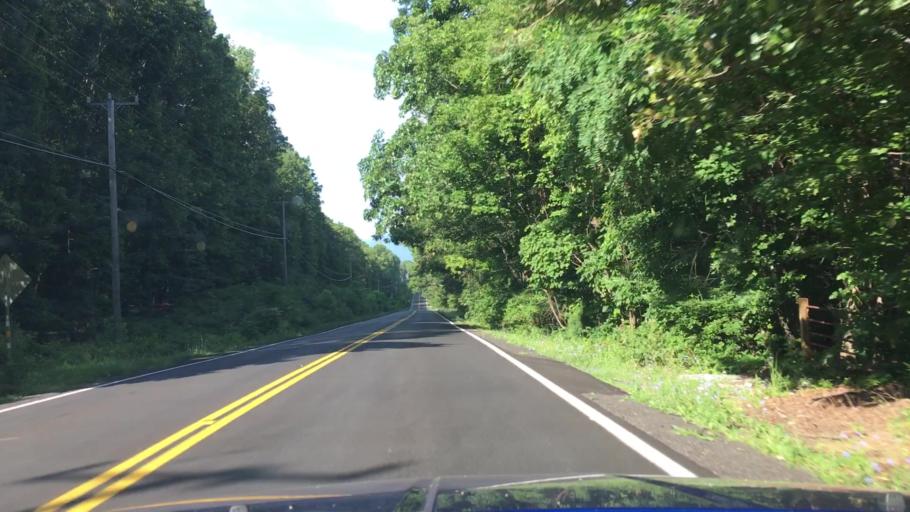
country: US
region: Virginia
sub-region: City of Waynesboro
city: Waynesboro
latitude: 38.0419
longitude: -78.9116
